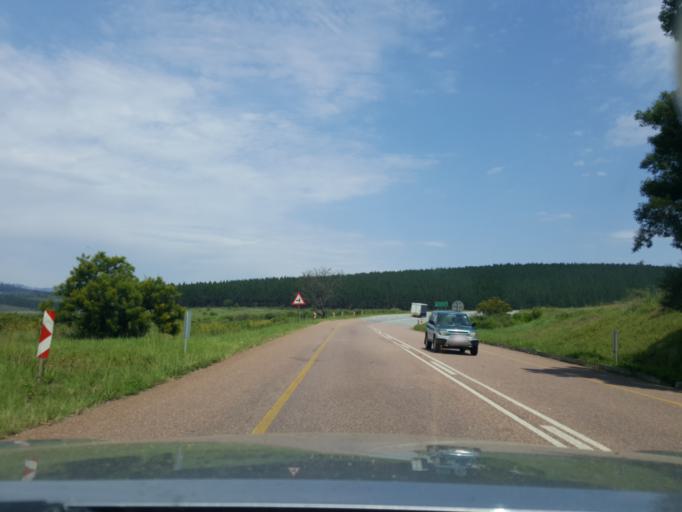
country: ZA
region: Mpumalanga
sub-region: Ehlanzeni District
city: White River
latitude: -25.1955
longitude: 31.0077
